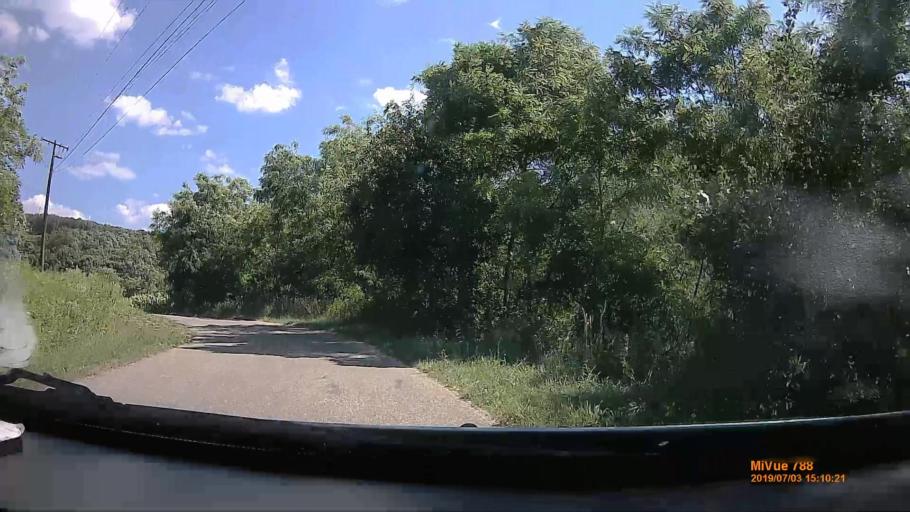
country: HU
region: Borsod-Abauj-Zemplen
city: Ozd
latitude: 48.2318
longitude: 20.3715
